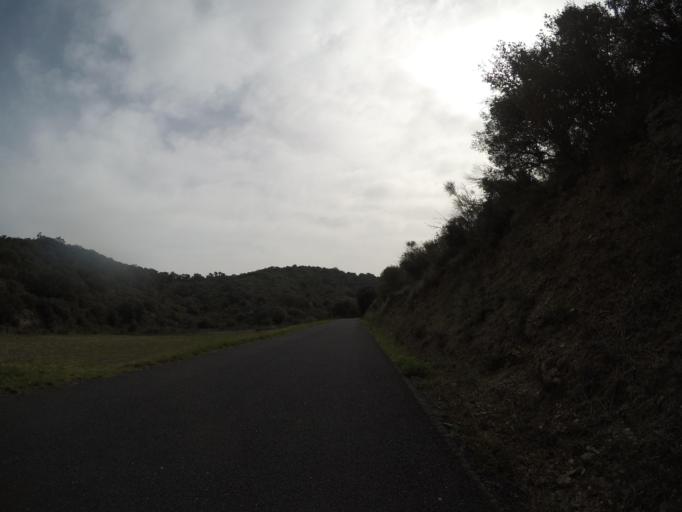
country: FR
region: Languedoc-Roussillon
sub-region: Departement des Pyrenees-Orientales
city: Estagel
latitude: 42.7545
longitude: 2.7165
